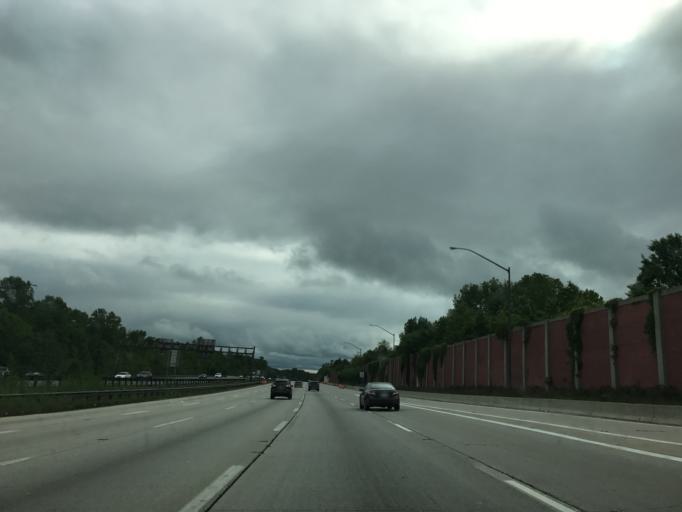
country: US
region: Maryland
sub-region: Prince George's County
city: Bowie
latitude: 38.9523
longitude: -76.7472
